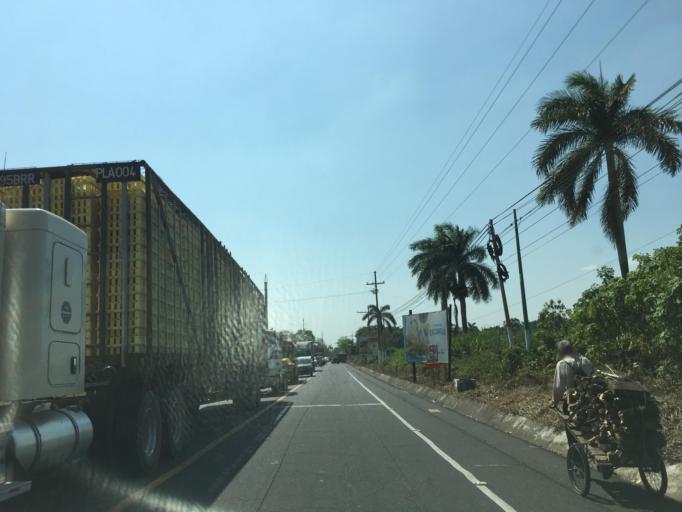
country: GT
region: Escuintla
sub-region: Municipio de Escuintla
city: Escuintla
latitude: 14.3296
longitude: -90.7975
